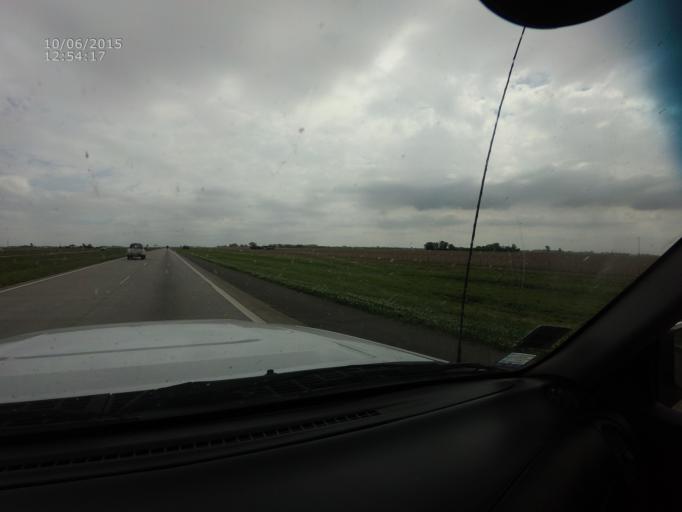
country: AR
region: Santa Fe
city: Armstrong
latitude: -32.8158
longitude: -61.5691
